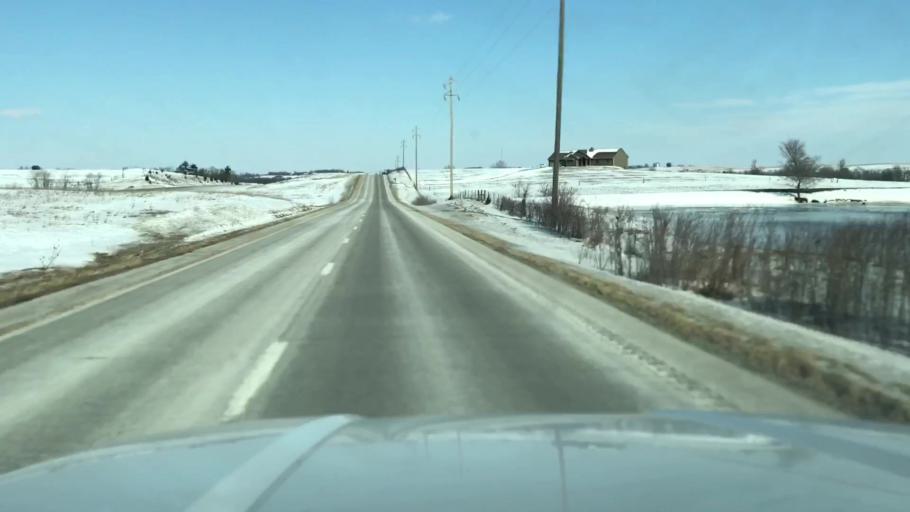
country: US
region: Missouri
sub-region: Andrew County
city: Savannah
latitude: 40.1297
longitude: -94.8695
